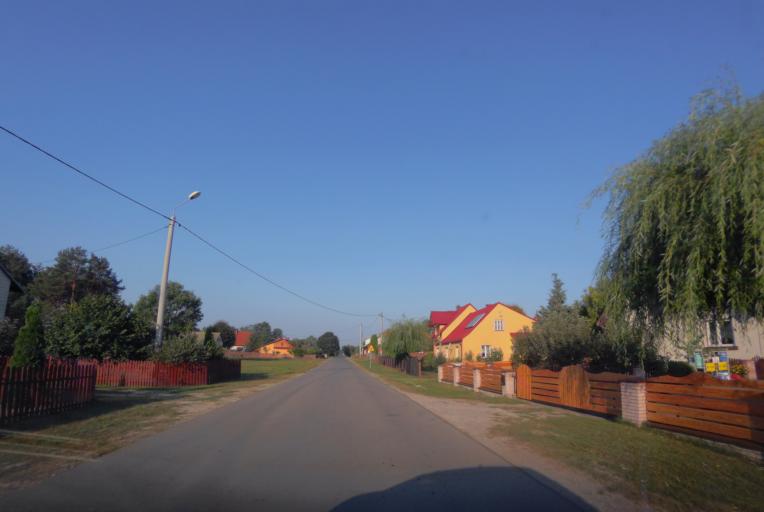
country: PL
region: Lublin Voivodeship
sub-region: Powiat janowski
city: Dzwola
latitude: 50.5826
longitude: 22.5724
